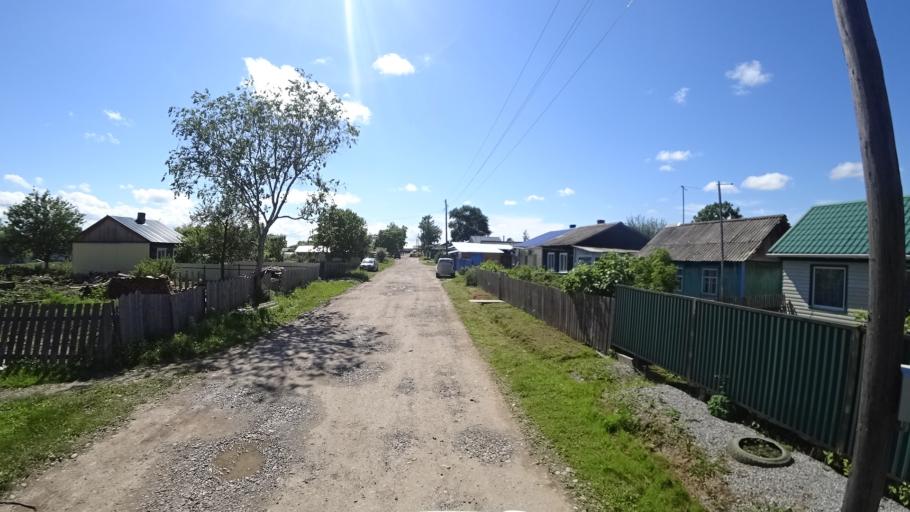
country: RU
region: Khabarovsk Krai
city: Khor
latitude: 47.8877
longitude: 135.0298
